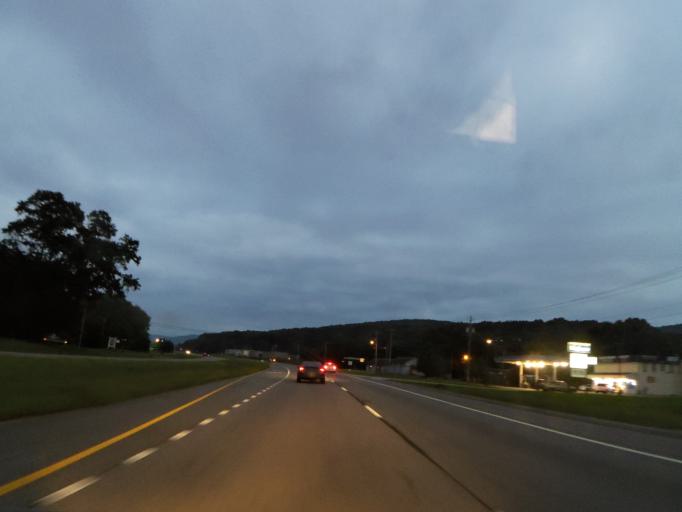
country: US
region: Alabama
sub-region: Madison County
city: Owens Cross Roads
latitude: 34.6953
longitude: -86.3745
